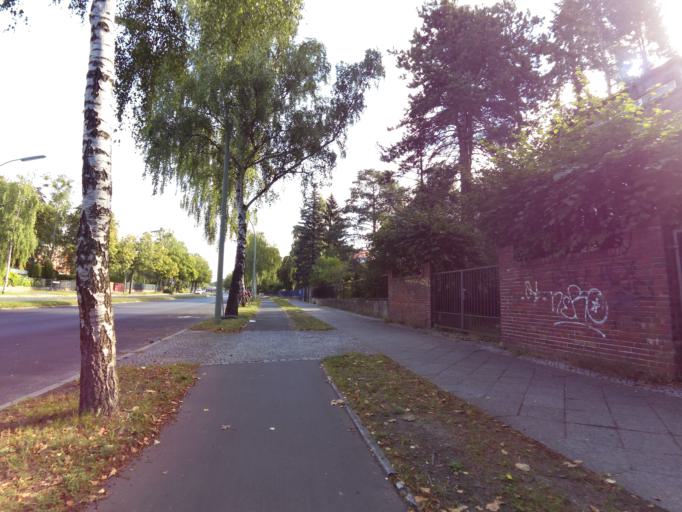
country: DE
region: Berlin
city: Zehlendorf Bezirk
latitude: 52.4403
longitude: 13.2371
